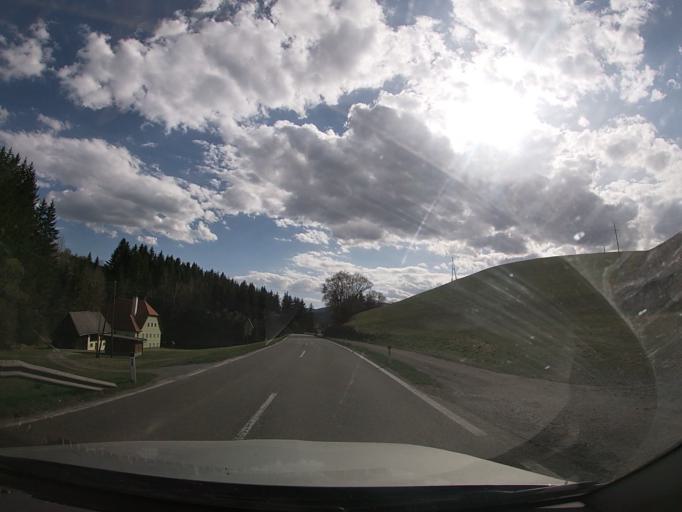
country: AT
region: Styria
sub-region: Politischer Bezirk Murau
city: Neumarkt in Steiermark
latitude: 47.0905
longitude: 14.4320
